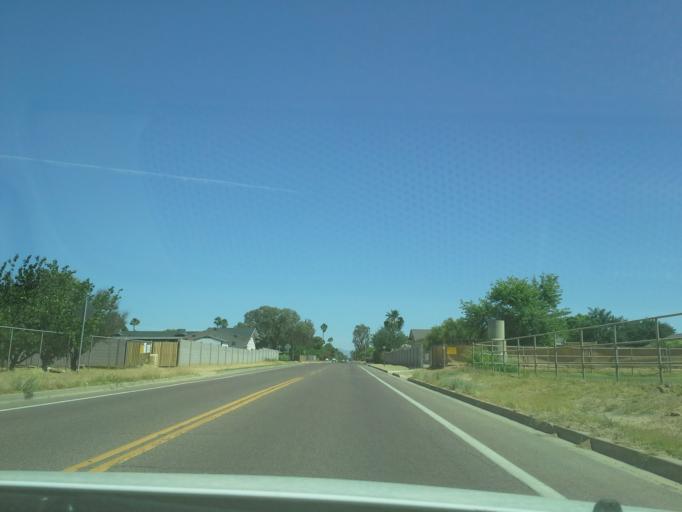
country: US
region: Arizona
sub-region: Maricopa County
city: Paradise Valley
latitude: 33.6048
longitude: -111.9692
